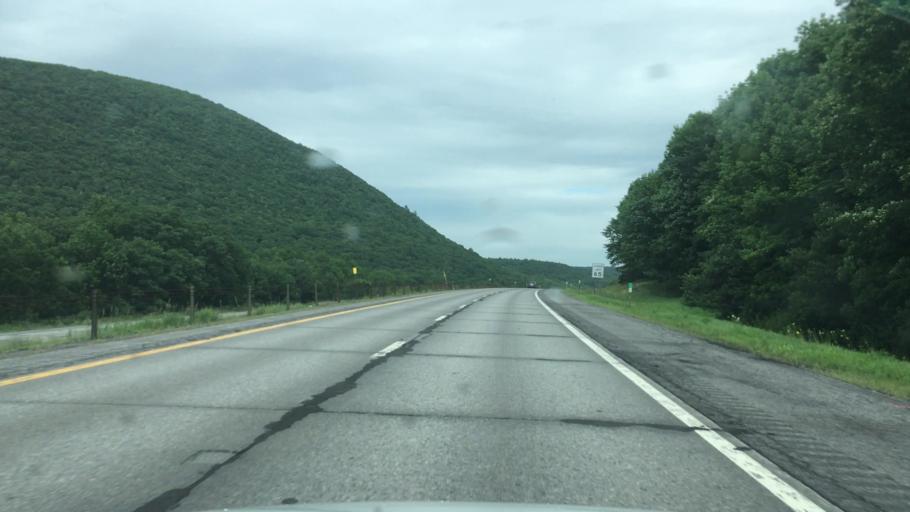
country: US
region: New York
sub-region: Otsego County
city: Worcester
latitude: 42.6442
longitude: -74.6465
